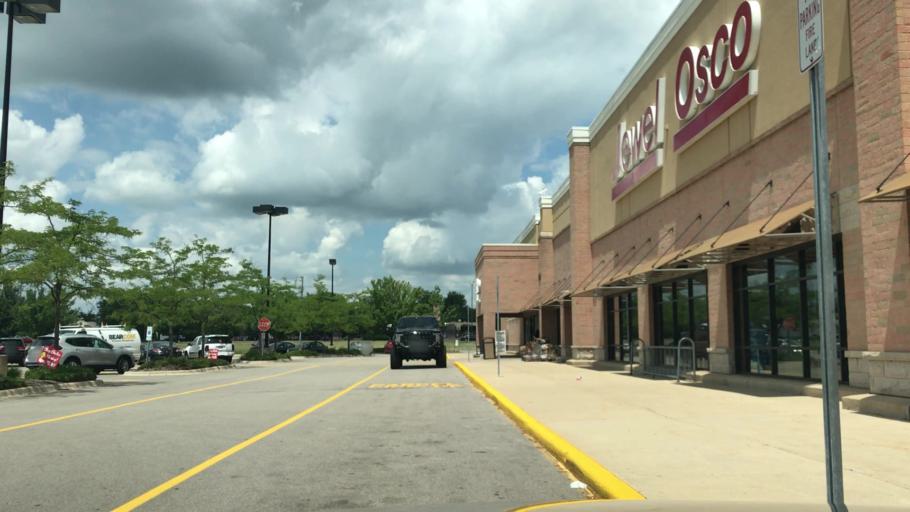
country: US
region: Illinois
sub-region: DuPage County
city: Warrenville
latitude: 41.7798
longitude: -88.2386
